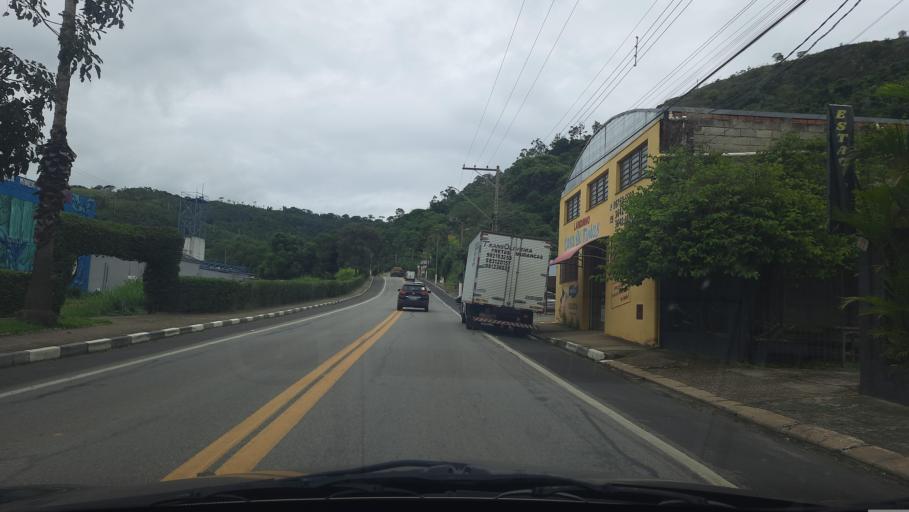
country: BR
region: Sao Paulo
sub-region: Sao Joao Da Boa Vista
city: Sao Joao da Boa Vista
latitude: -21.9412
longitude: -46.7156
